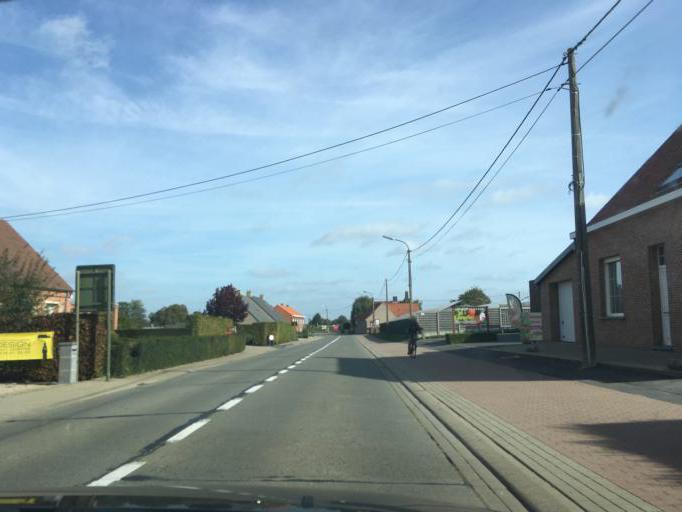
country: BE
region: Flanders
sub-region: Provincie West-Vlaanderen
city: Moorslede
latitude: 50.9037
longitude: 3.0715
